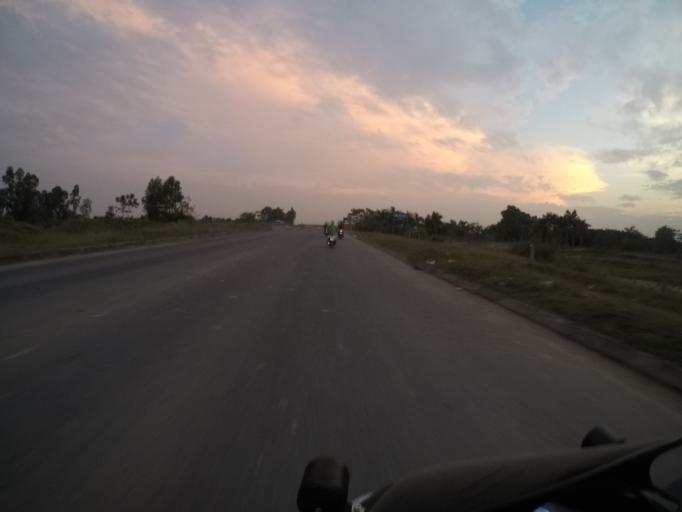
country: VN
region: Vinh Phuc
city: Phuc Yen
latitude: 21.2629
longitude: 105.7231
